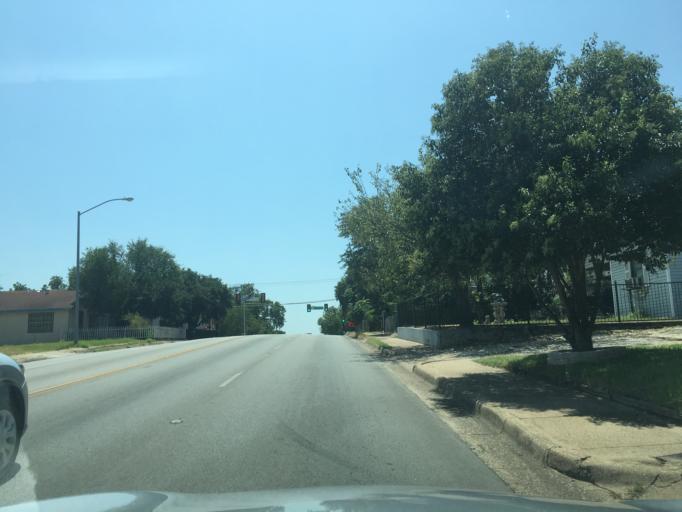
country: US
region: Texas
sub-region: Tarrant County
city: Edgecliff Village
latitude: 32.6827
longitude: -97.3531
